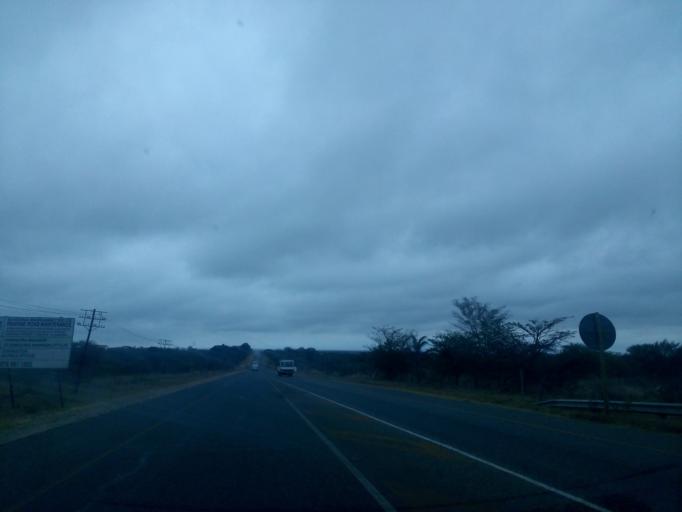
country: ZA
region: Limpopo
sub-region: Vhembe District Municipality
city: Louis Trichardt
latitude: -23.0806
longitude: 29.9079
